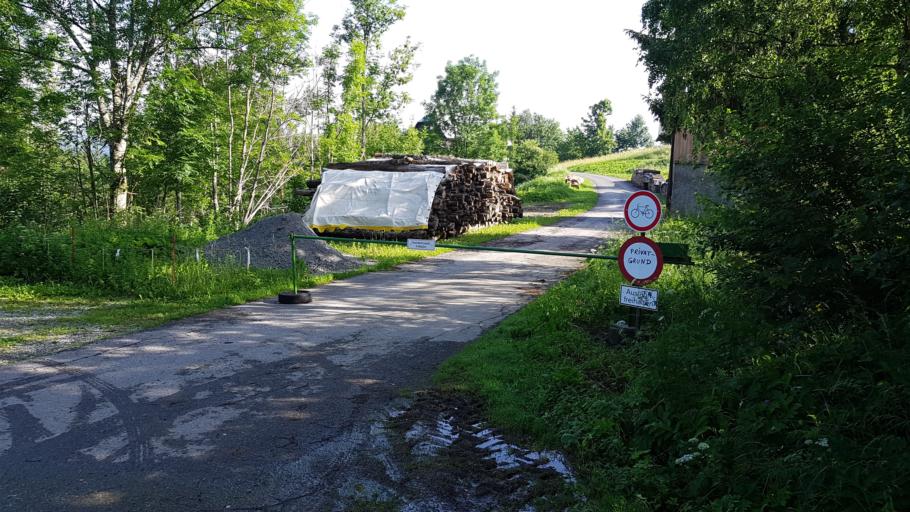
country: AT
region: Styria
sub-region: Politischer Bezirk Graz-Umgebung
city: Rothelstein
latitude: 47.3743
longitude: 15.4224
